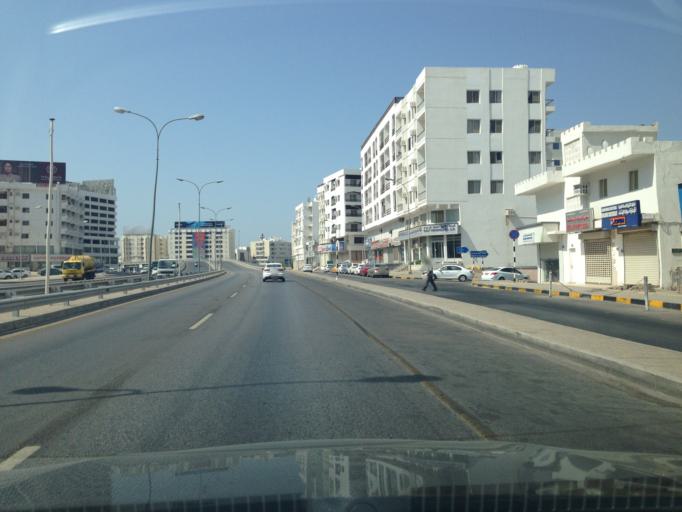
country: OM
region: Muhafazat Masqat
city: Muscat
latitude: 23.5904
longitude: 58.5420
